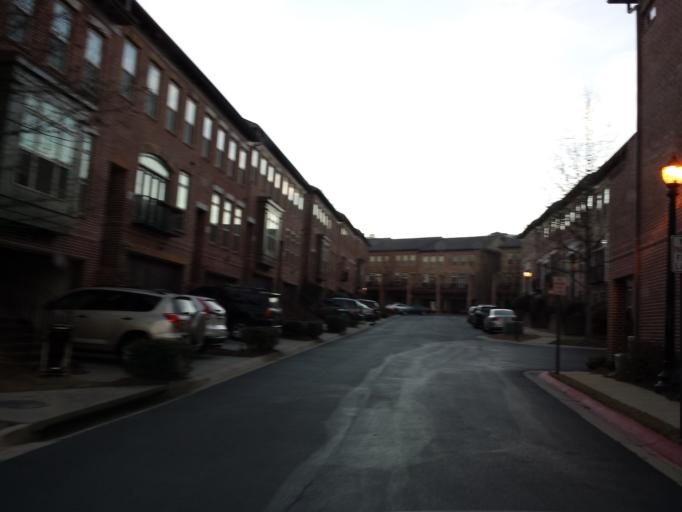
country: US
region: Georgia
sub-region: Cobb County
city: Vinings
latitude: 33.8929
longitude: -84.4721
